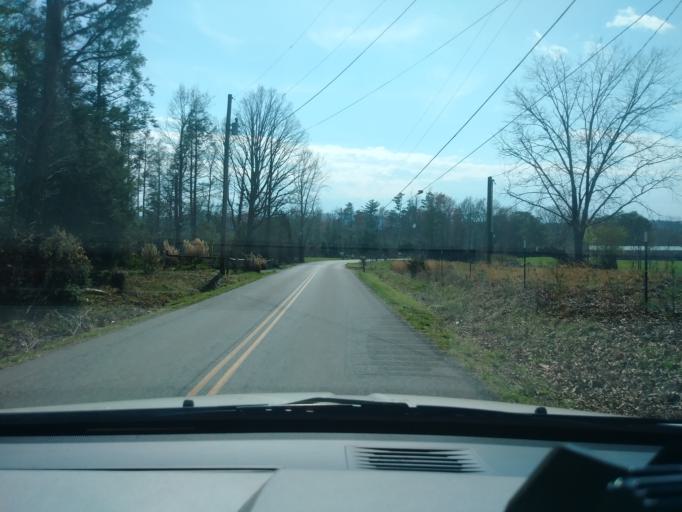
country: US
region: Tennessee
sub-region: Greene County
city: Greeneville
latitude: 36.0661
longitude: -82.7901
